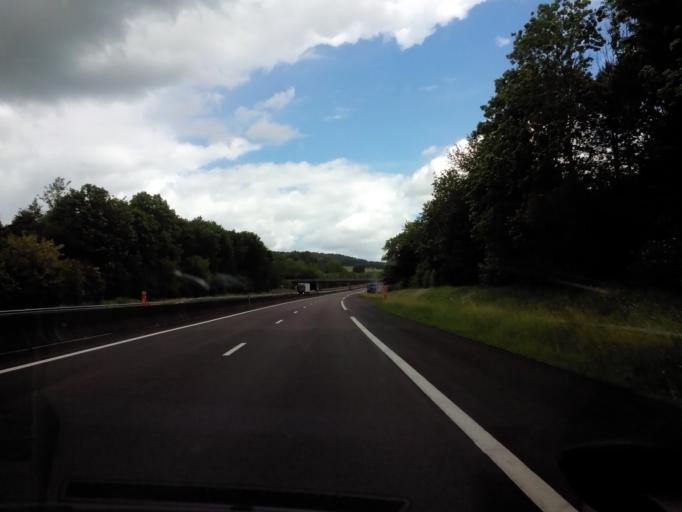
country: FR
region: Champagne-Ardenne
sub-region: Departement de la Haute-Marne
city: Rolampont
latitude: 47.9432
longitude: 5.3014
